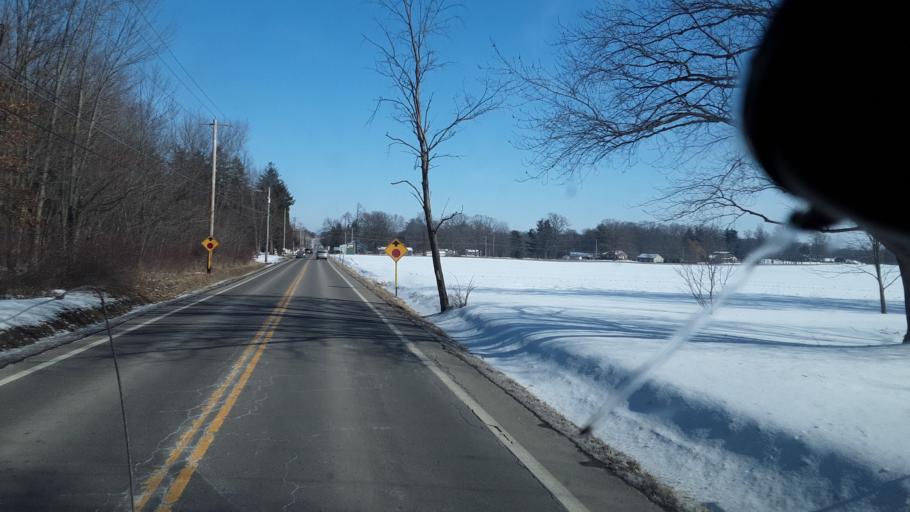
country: US
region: Ohio
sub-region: Columbiana County
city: Leetonia
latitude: 40.9442
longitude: -80.7374
